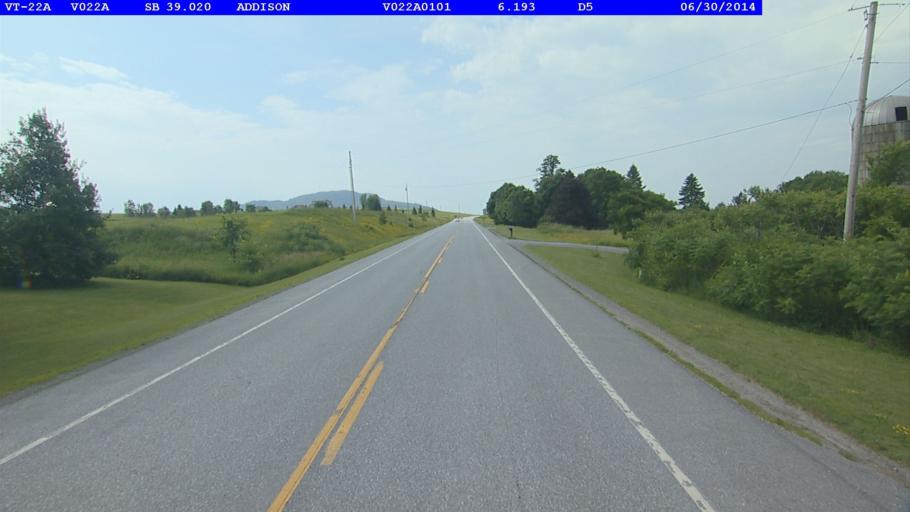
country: US
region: Vermont
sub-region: Addison County
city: Vergennes
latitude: 44.1179
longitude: -73.2936
